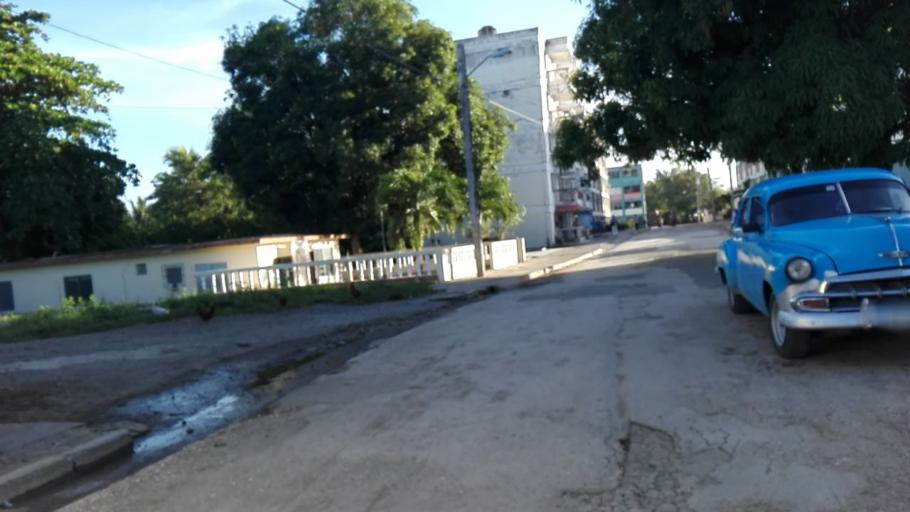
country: CU
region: Granma
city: Bartolome Maso
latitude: 20.1663
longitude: -76.9461
